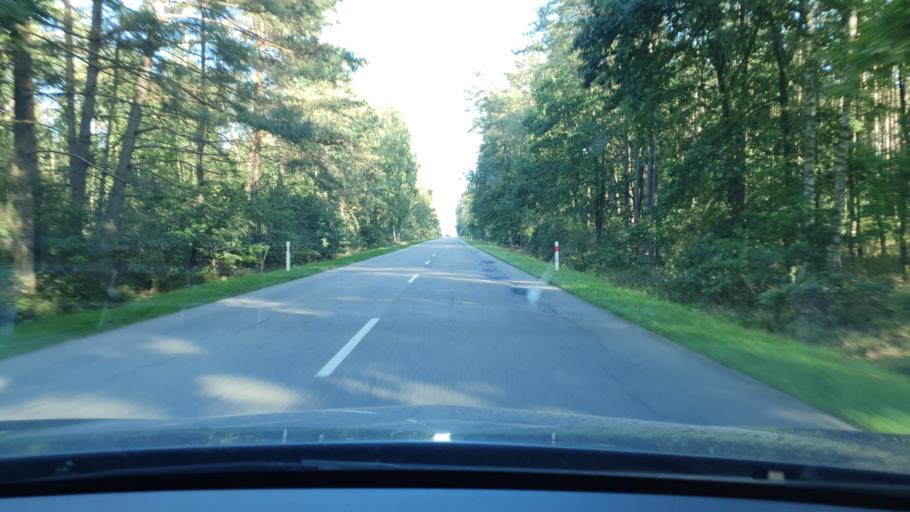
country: PL
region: West Pomeranian Voivodeship
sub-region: Powiat kamienski
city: Golczewo
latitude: 53.8129
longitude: 15.0913
